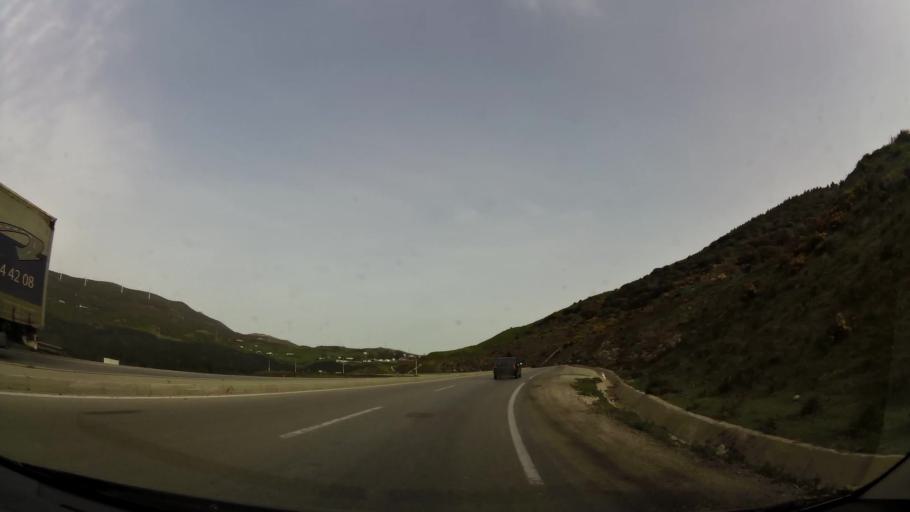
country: MA
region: Tanger-Tetouan
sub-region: Tanger-Assilah
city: Dar Chaoui
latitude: 35.5659
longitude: -5.5898
